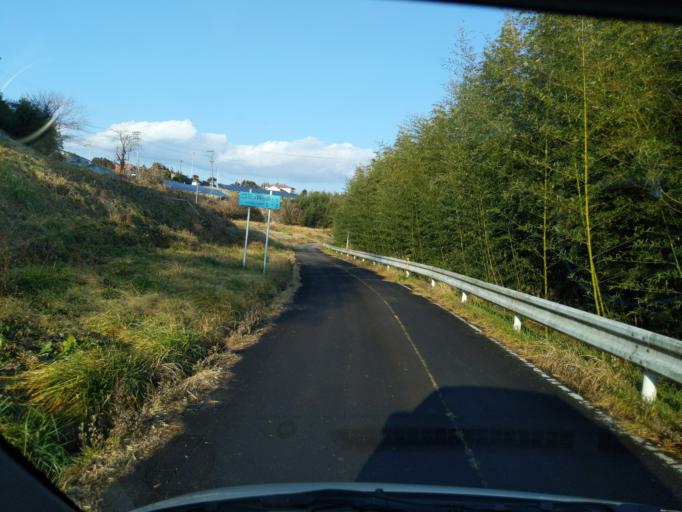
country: JP
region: Miyagi
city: Wakuya
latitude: 38.7034
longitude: 141.1362
